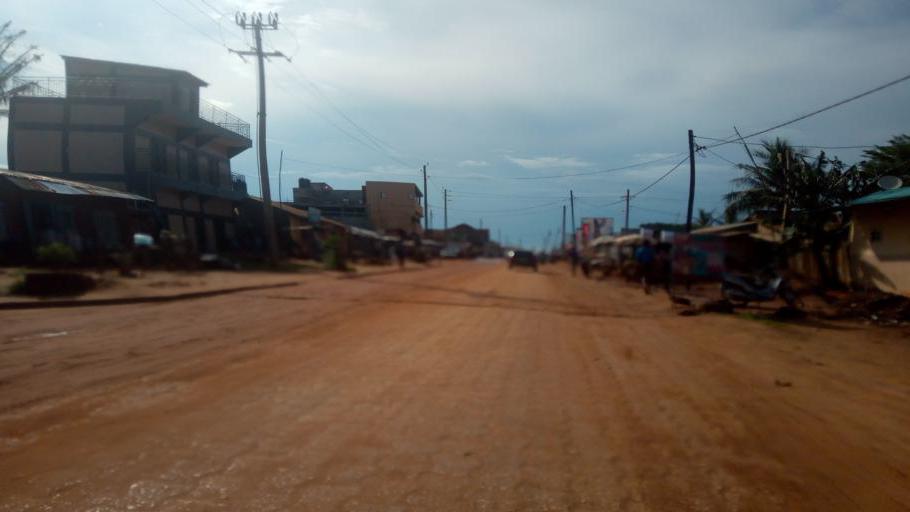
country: BJ
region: Atlantique
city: Abomey-Calavi
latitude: 6.4527
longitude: 2.3388
